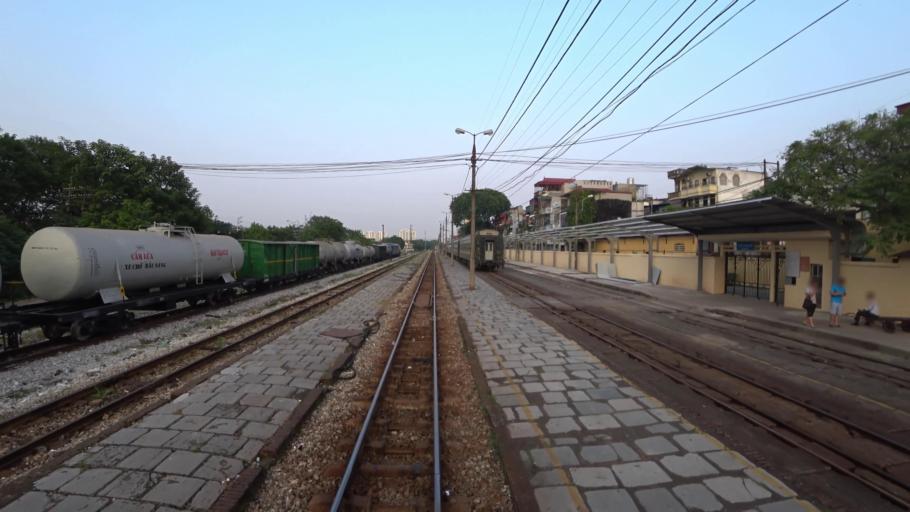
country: VN
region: Ha Noi
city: Hoan Kiem
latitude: 21.0629
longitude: 105.8943
